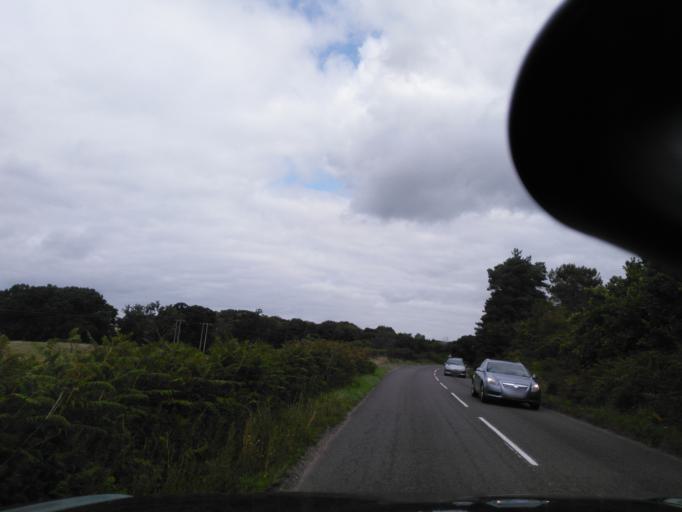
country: GB
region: England
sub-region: Dorset
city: Wareham
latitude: 50.7310
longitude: -2.1168
